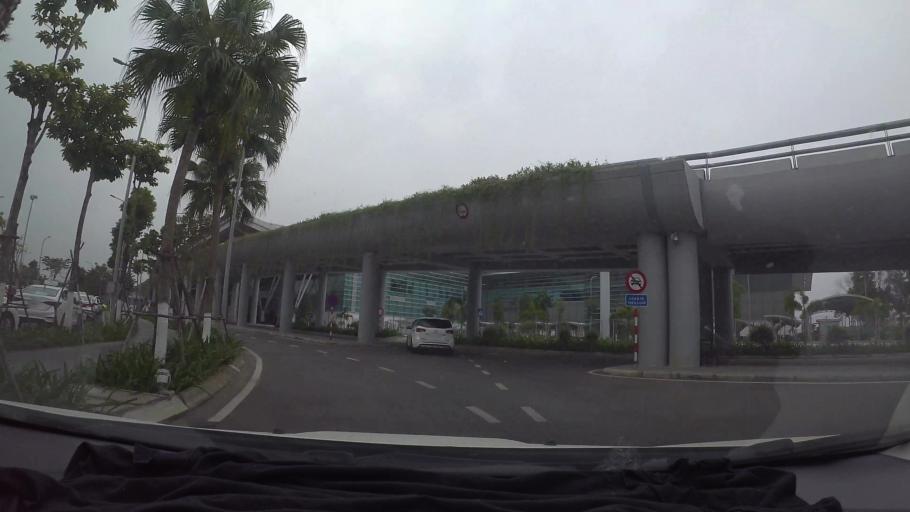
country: VN
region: Da Nang
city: Thanh Khe
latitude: 16.0578
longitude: 108.2029
